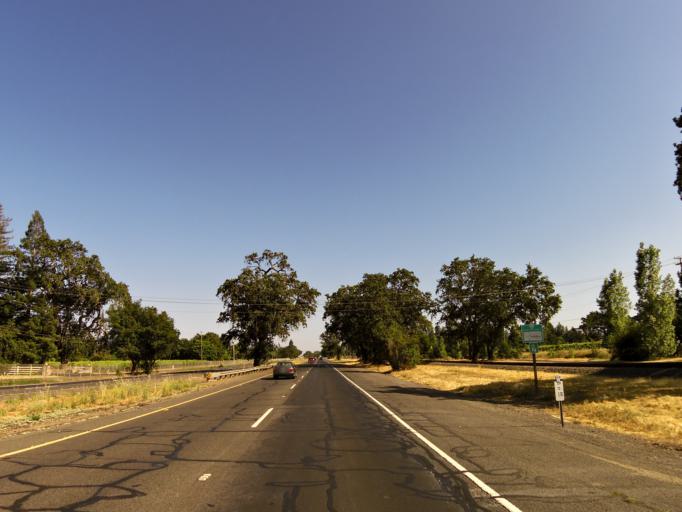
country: US
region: California
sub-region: Napa County
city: Yountville
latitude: 38.3722
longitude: -122.3416
